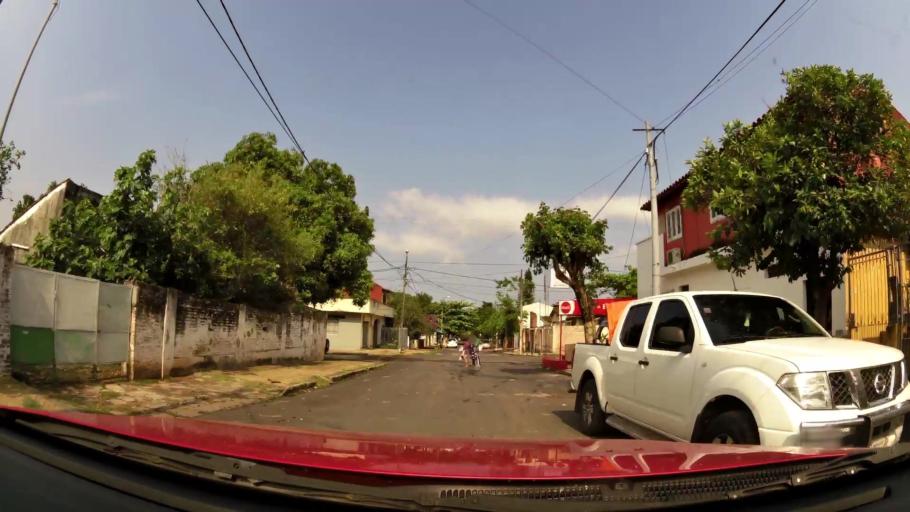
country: PY
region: Asuncion
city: Asuncion
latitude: -25.2945
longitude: -57.6607
